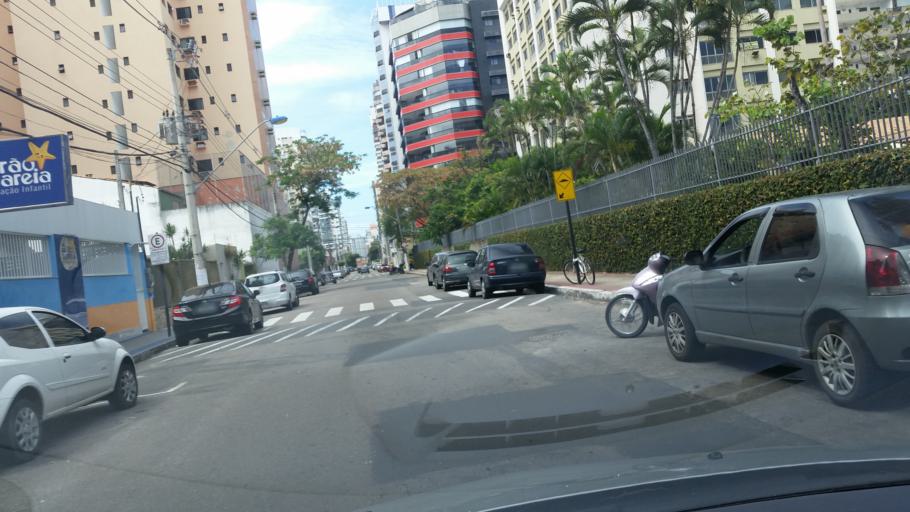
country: BR
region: Espirito Santo
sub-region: Vila Velha
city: Vila Velha
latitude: -20.3421
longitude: -40.2861
